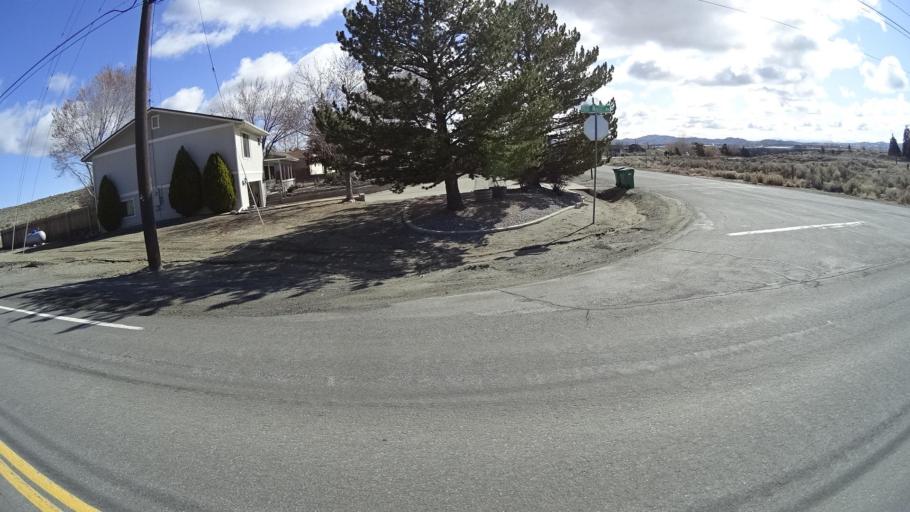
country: US
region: Nevada
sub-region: Washoe County
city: Cold Springs
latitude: 39.6676
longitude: -119.9224
